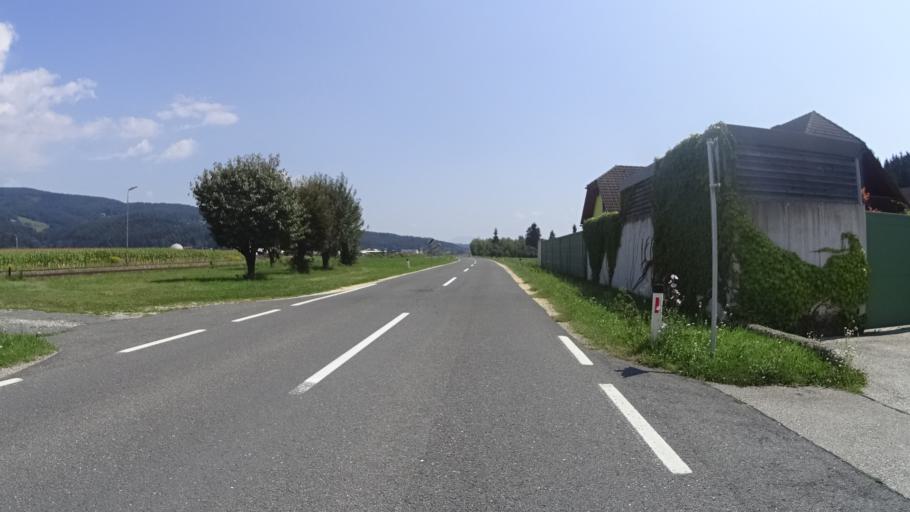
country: AT
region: Carinthia
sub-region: Politischer Bezirk Volkermarkt
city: Bleiburg/Pliberk
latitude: 46.5729
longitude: 14.7922
